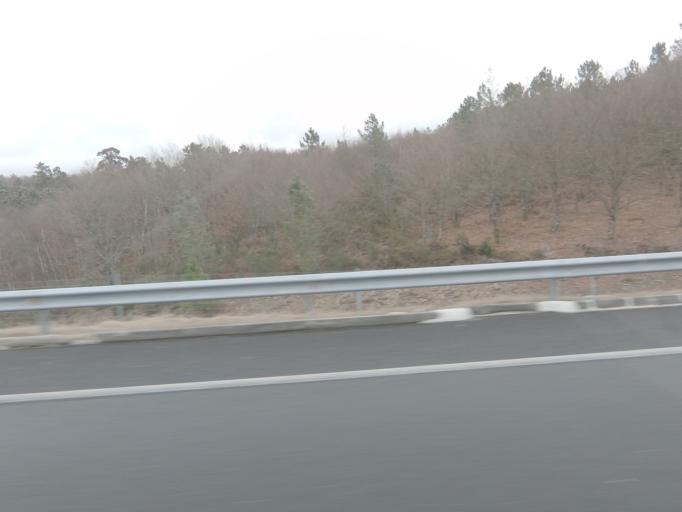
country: ES
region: Galicia
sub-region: Provincia de Pontevedra
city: Lalin
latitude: 42.6048
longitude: -8.0994
